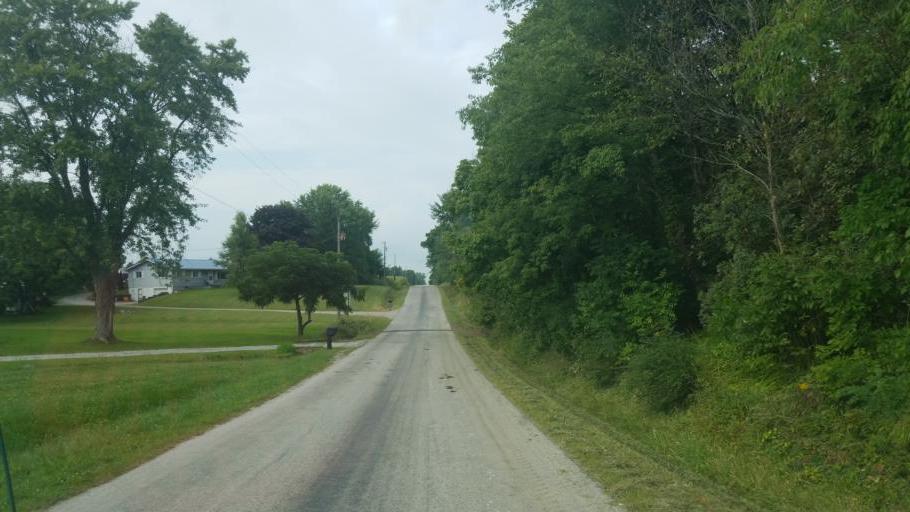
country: US
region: Ohio
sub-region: Wayne County
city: West Salem
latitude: 40.9532
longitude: -82.0535
